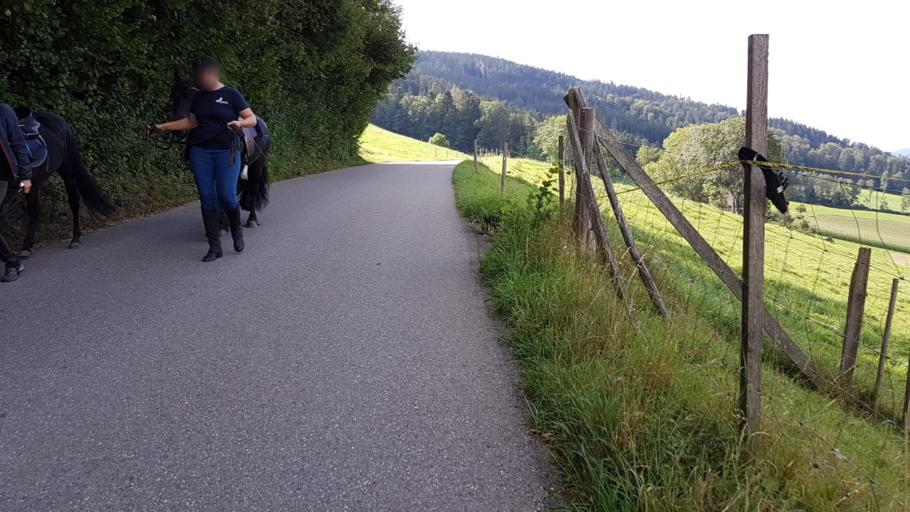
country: CH
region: Bern
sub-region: Bern-Mittelland District
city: Konolfingen
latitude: 46.8660
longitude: 7.6326
